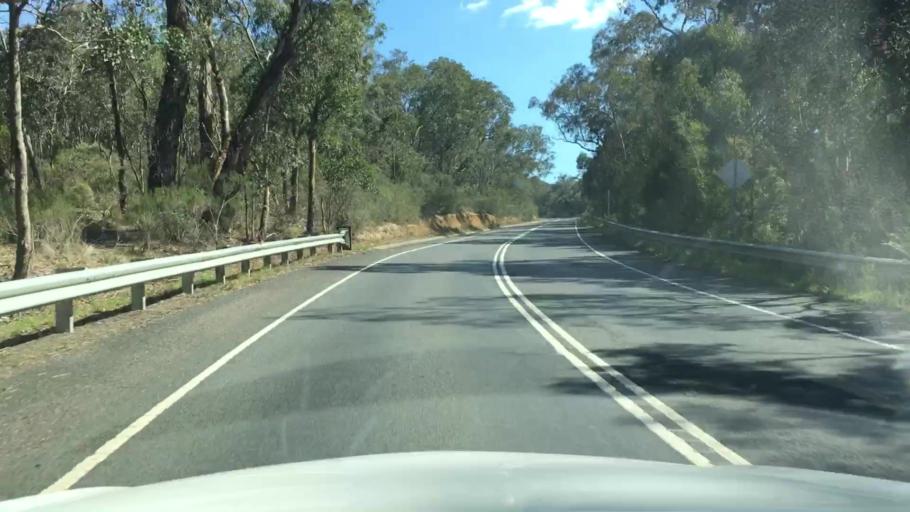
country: AU
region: Victoria
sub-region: Nillumbik
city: North Warrandyte
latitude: -37.6755
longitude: 145.2460
